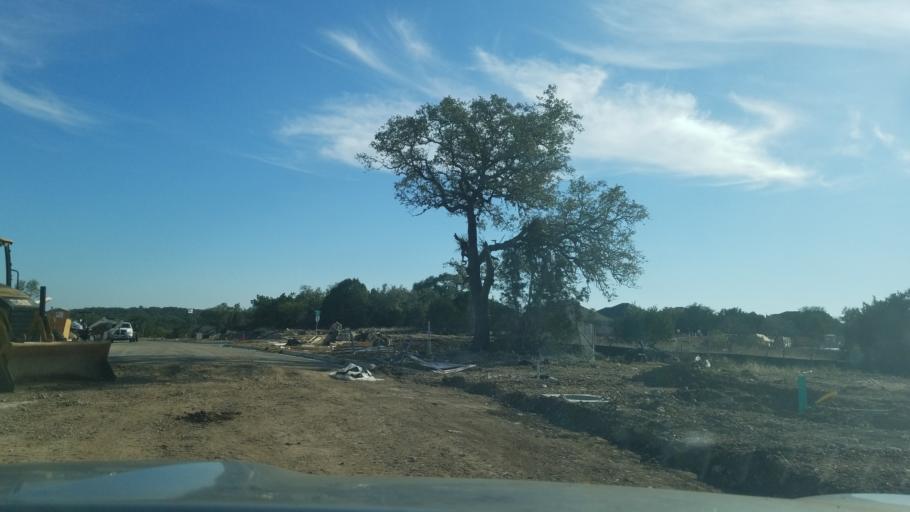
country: US
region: Texas
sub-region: Comal County
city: Canyon Lake
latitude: 29.7826
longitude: -98.2860
